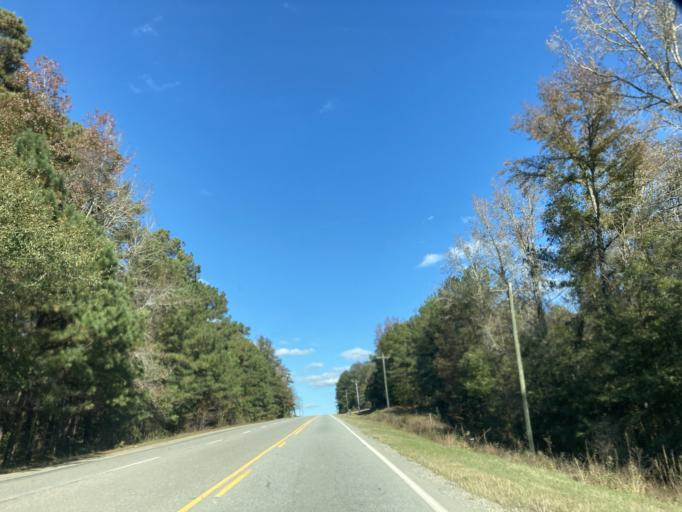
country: US
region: Georgia
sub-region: Jones County
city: Gray
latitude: 32.9093
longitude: -83.5201
